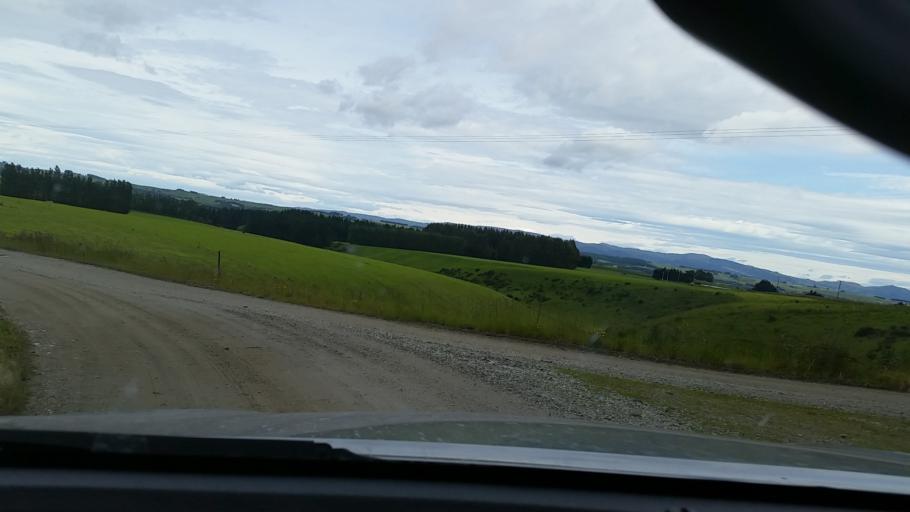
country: NZ
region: Southland
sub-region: Gore District
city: Gore
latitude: -46.2472
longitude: 168.8640
